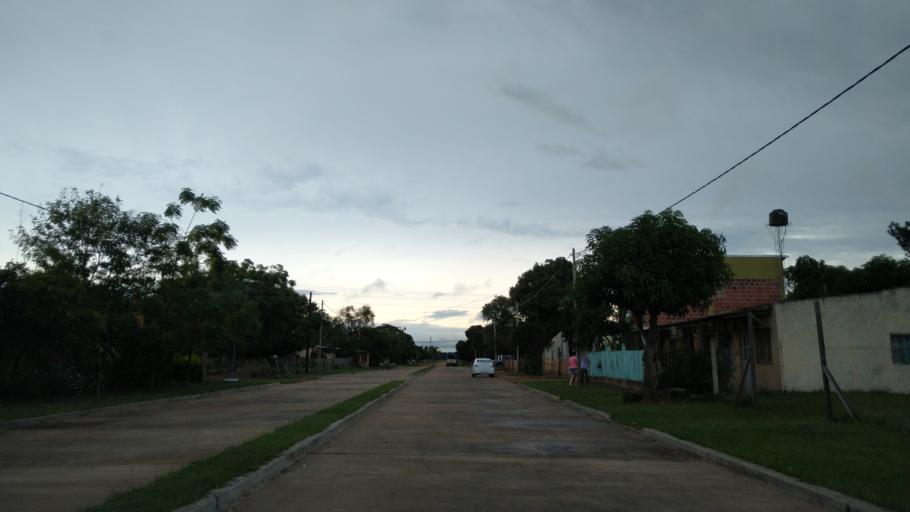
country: PY
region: Misiones
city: Ayolas
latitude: -27.6309
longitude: -56.9081
